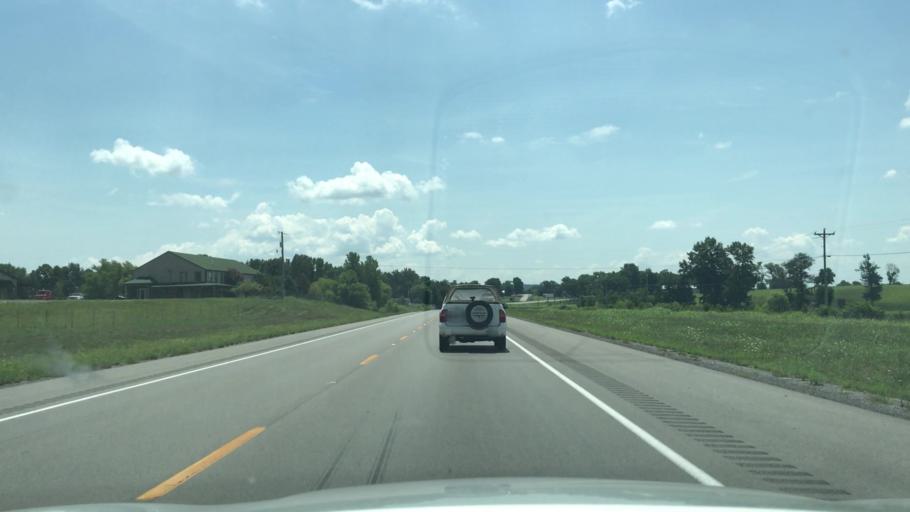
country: US
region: Tennessee
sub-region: Pickett County
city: Byrdstown
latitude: 36.6301
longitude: -85.0935
